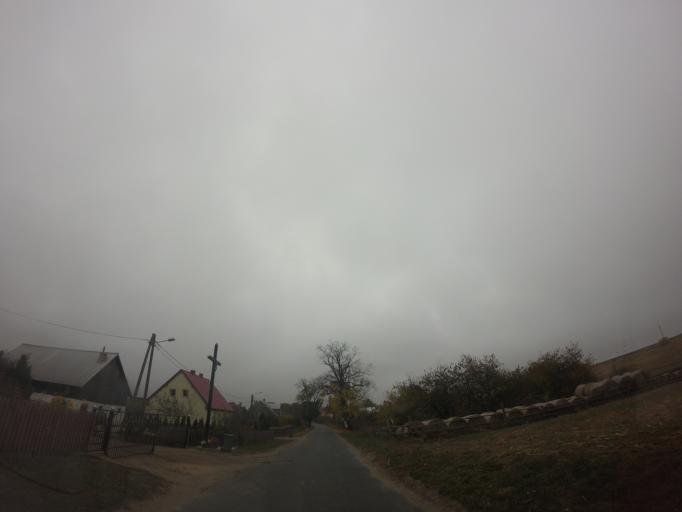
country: PL
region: West Pomeranian Voivodeship
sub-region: Powiat choszczenski
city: Choszczno
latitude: 53.1108
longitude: 15.4037
